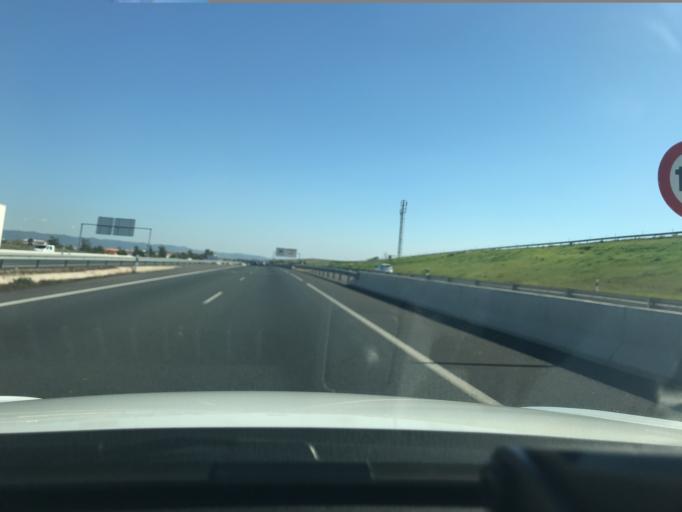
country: ES
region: Andalusia
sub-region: Province of Cordoba
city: Cordoba
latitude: 37.8532
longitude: -4.7805
